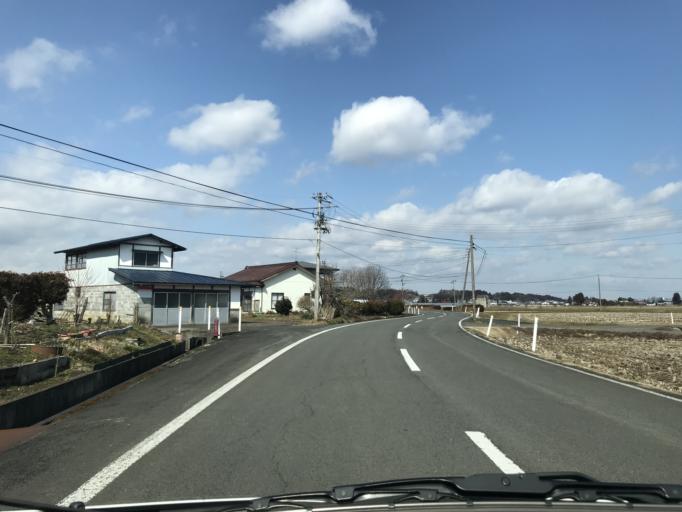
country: JP
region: Iwate
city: Mizusawa
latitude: 39.1001
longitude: 141.1527
